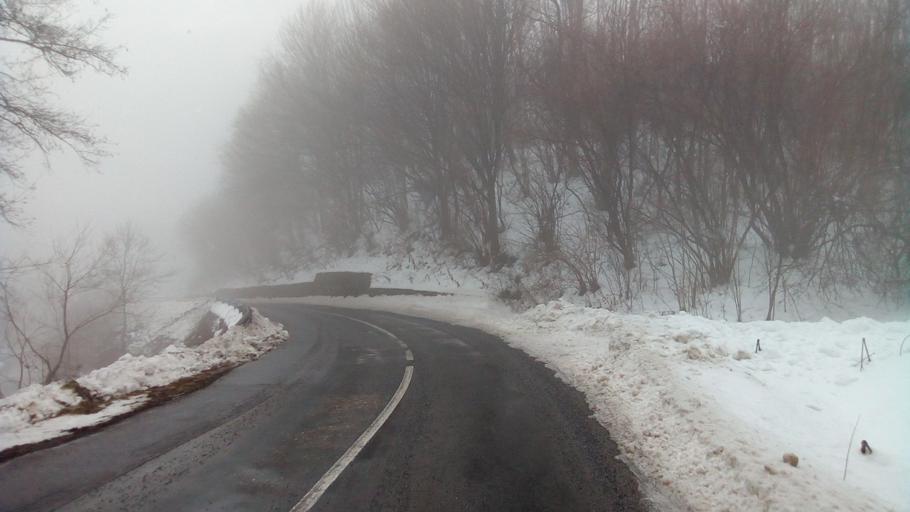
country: HR
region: Sisacko-Moslavacka
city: Petrinja
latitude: 45.3735
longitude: 16.2822
